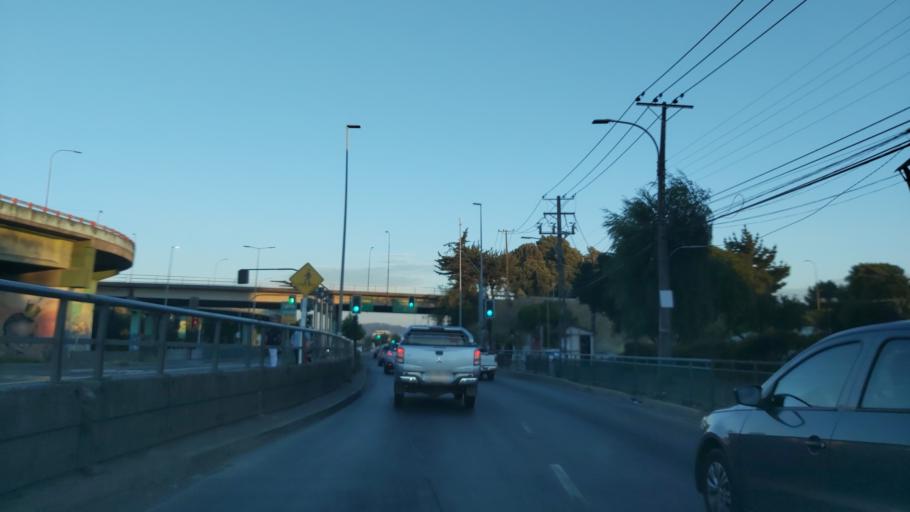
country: CL
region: Biobio
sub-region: Provincia de Concepcion
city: Concepcion
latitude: -36.8386
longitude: -73.1021
